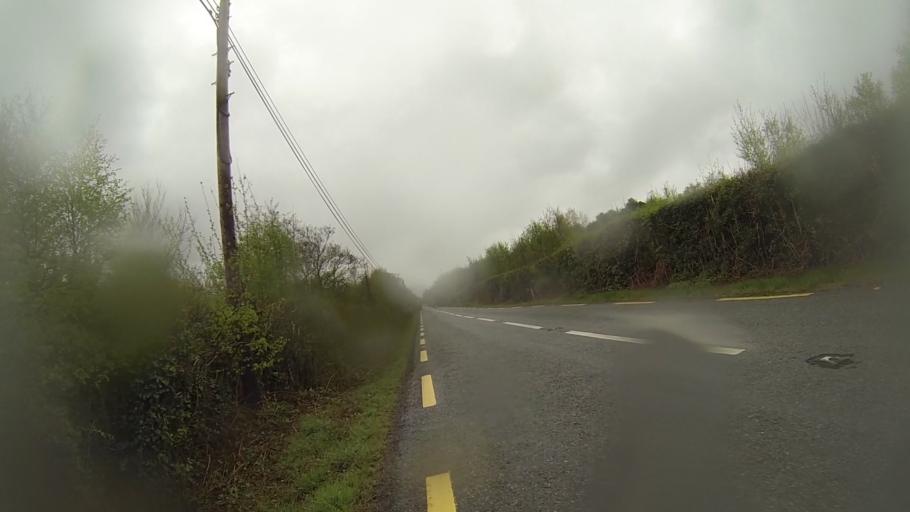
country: IE
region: Munster
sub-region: Ciarrai
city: Kenmare
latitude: 51.8212
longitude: -9.5288
